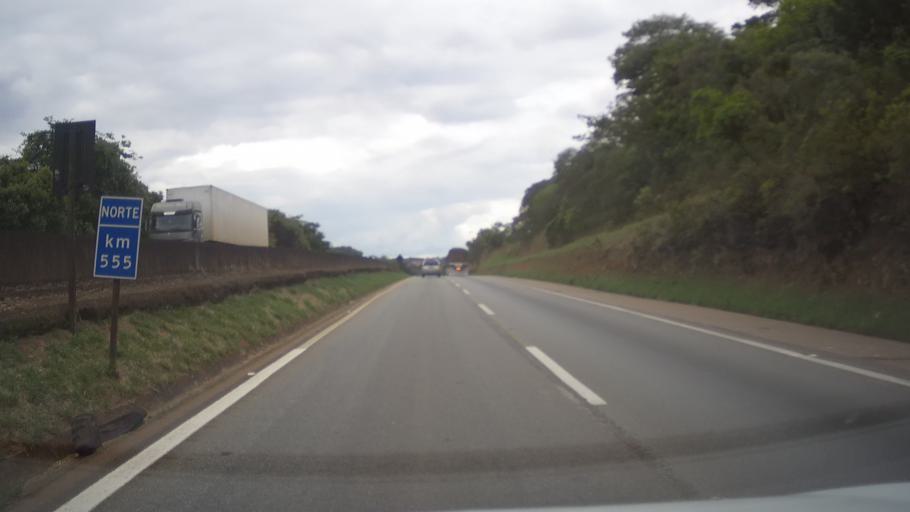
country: BR
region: Minas Gerais
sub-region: Itauna
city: Itauna
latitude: -20.3354
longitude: -44.4470
